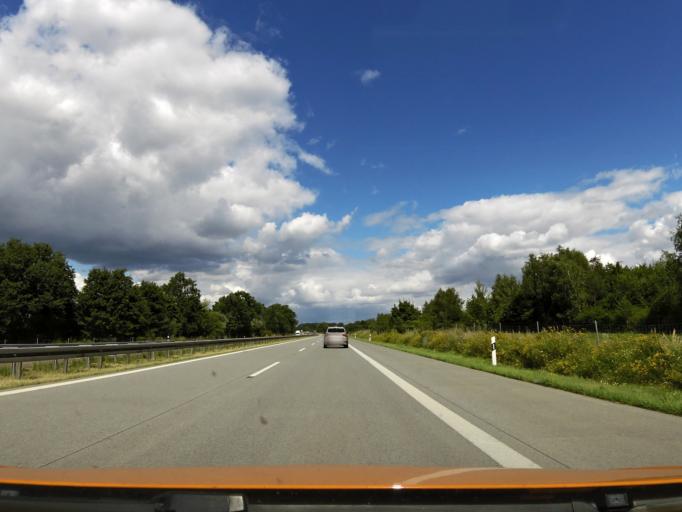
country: DE
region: Brandenburg
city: Althuttendorf
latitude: 52.9746
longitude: 13.8175
